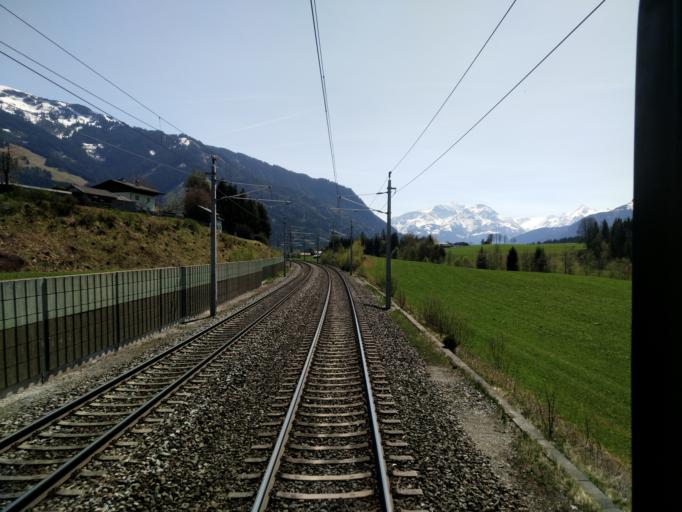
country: AT
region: Salzburg
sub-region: Politischer Bezirk Zell am See
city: Saalfelden am Steinernen Meer
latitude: 47.4010
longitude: 12.8297
